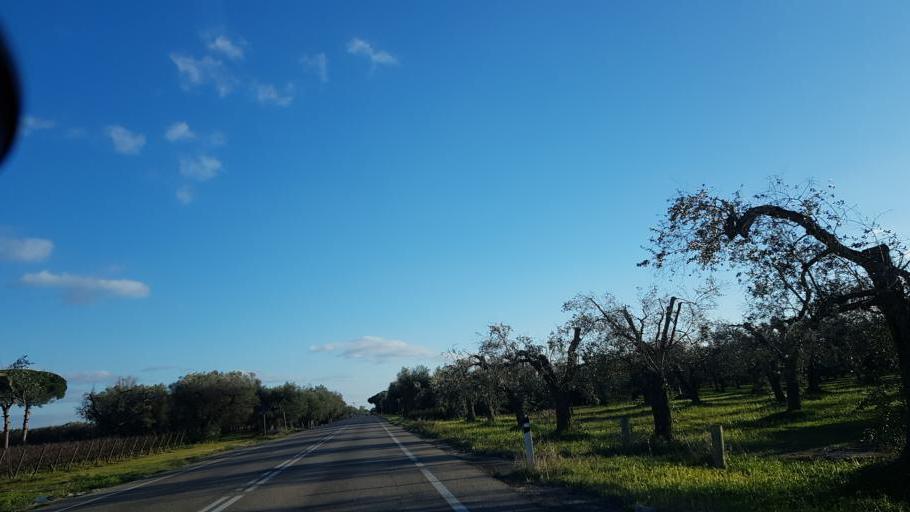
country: IT
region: Apulia
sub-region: Provincia di Lecce
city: Squinzano
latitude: 40.4558
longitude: 18.0244
